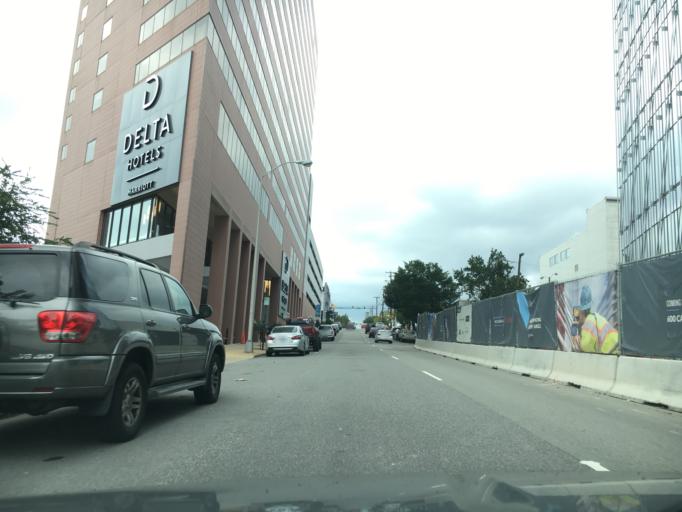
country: US
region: Virginia
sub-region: City of Richmond
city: Richmond
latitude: 37.5378
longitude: -77.4400
